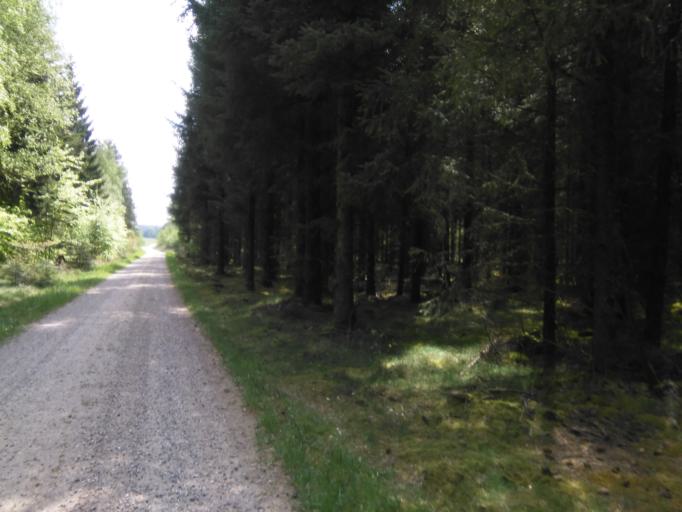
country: DK
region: Central Jutland
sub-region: Silkeborg Kommune
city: Svejbaek
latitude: 56.0560
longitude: 9.6600
